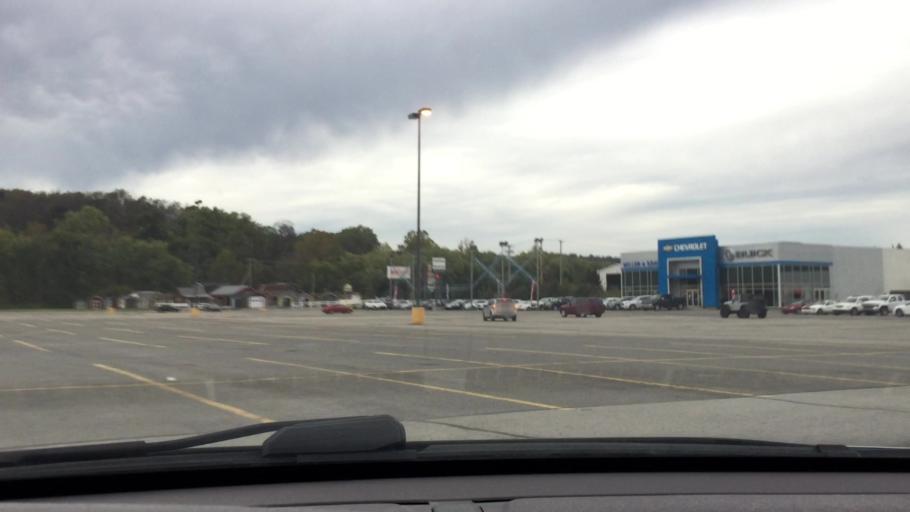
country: US
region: Pennsylvania
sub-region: Beaver County
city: Aliquippa
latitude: 40.5978
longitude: -80.3038
